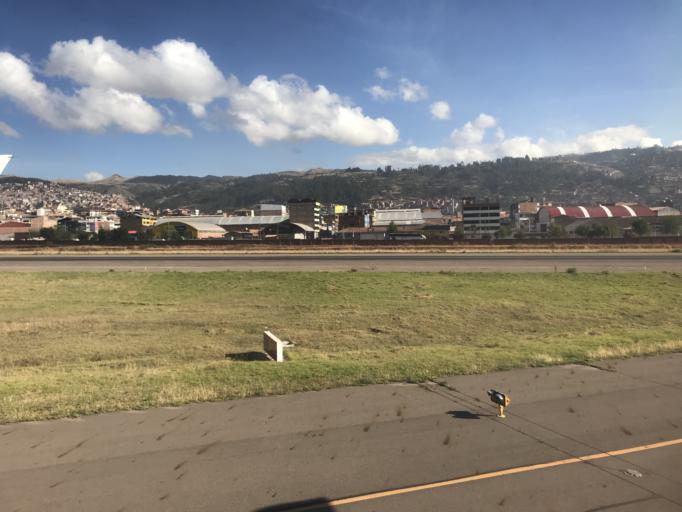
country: PE
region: Cusco
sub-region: Provincia de Cusco
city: Cusco
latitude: -13.5363
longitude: -71.9410
